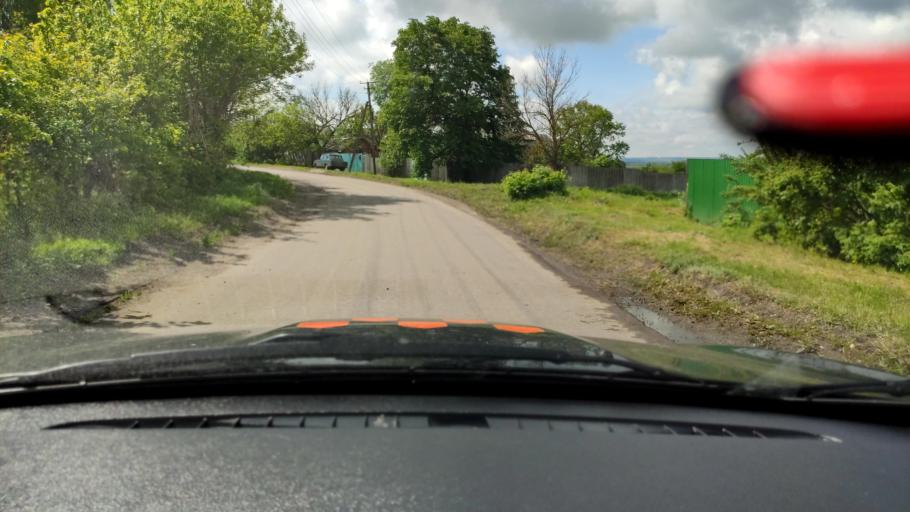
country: RU
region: Voronezj
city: Uryv-Pokrovka
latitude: 51.1078
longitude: 39.1649
